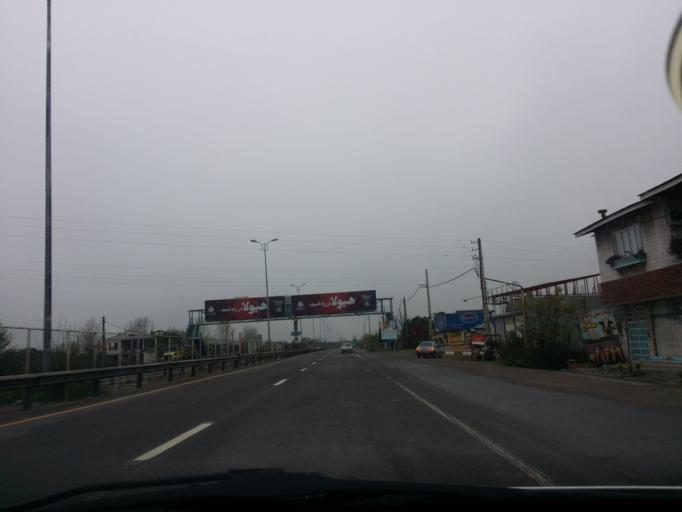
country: IR
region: Mazandaran
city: Tonekabon
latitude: 36.8142
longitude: 50.8539
